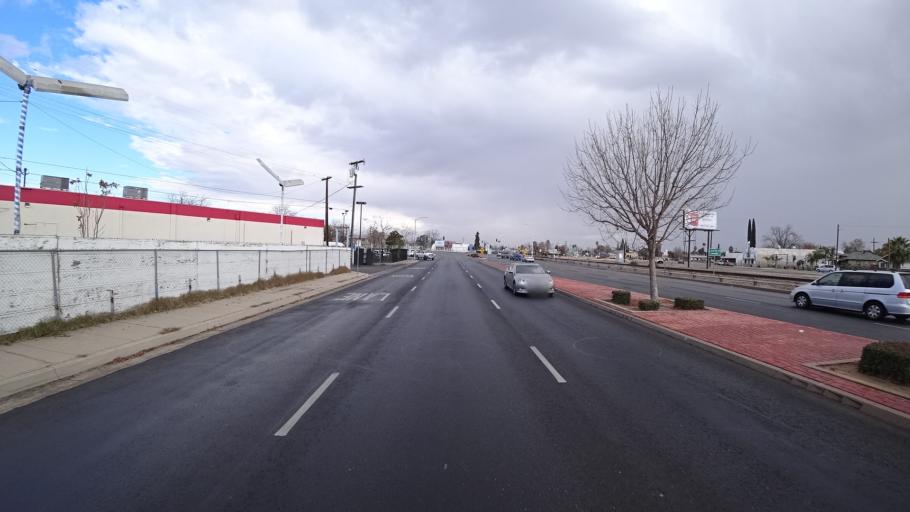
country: US
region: California
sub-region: Kern County
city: Bakersfield
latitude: 35.3738
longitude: -118.9931
